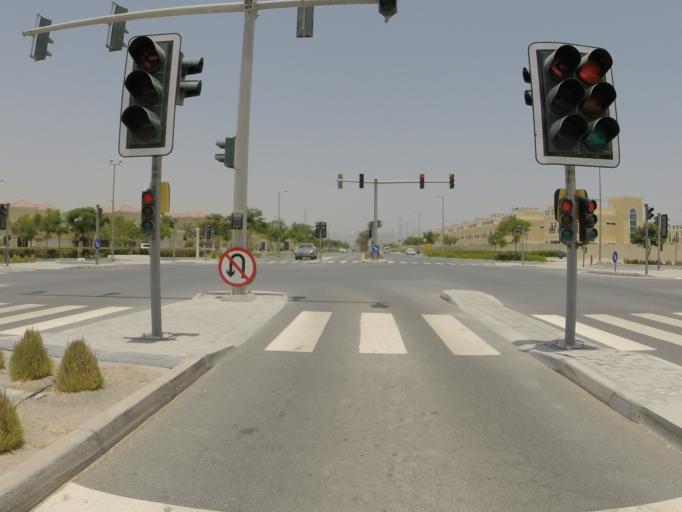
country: AE
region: Dubai
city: Dubai
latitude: 25.0414
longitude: 55.1705
